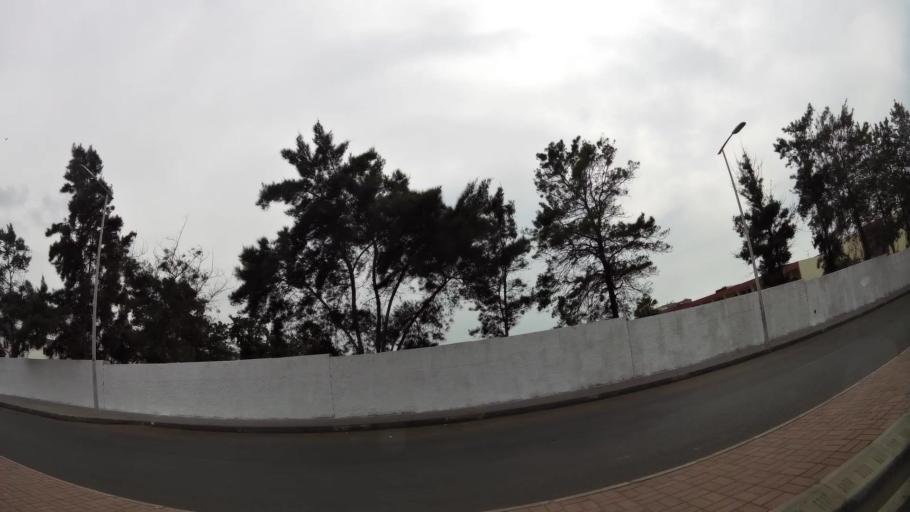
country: MA
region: Rabat-Sale-Zemmour-Zaer
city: Sale
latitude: 34.0399
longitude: -6.8095
